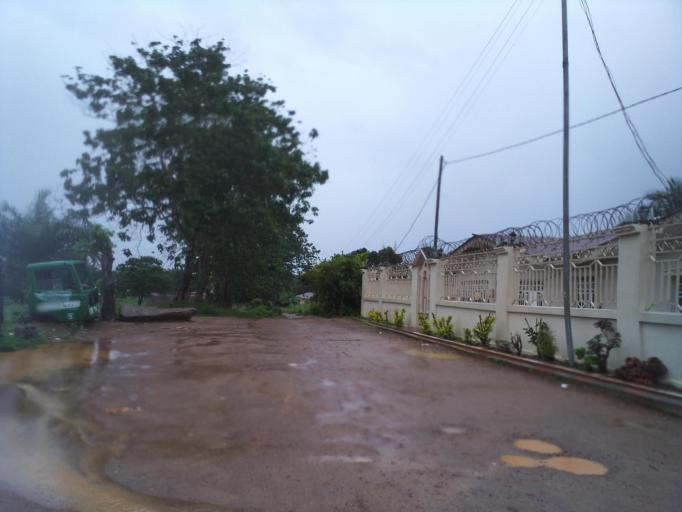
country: SL
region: Eastern Province
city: Kenema
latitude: 7.8560
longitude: -11.1932
